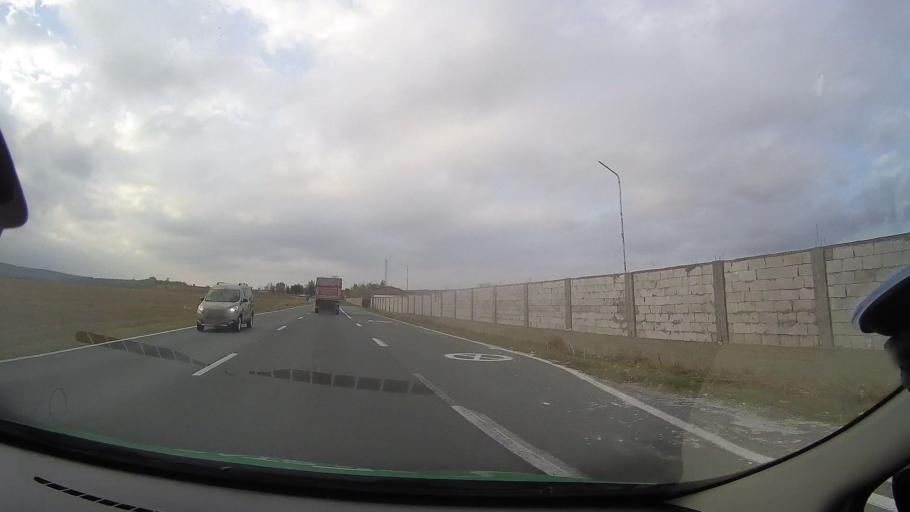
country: RO
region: Constanta
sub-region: Comuna Mircea Voda
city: Mircea Voda
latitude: 44.2700
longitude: 28.1753
